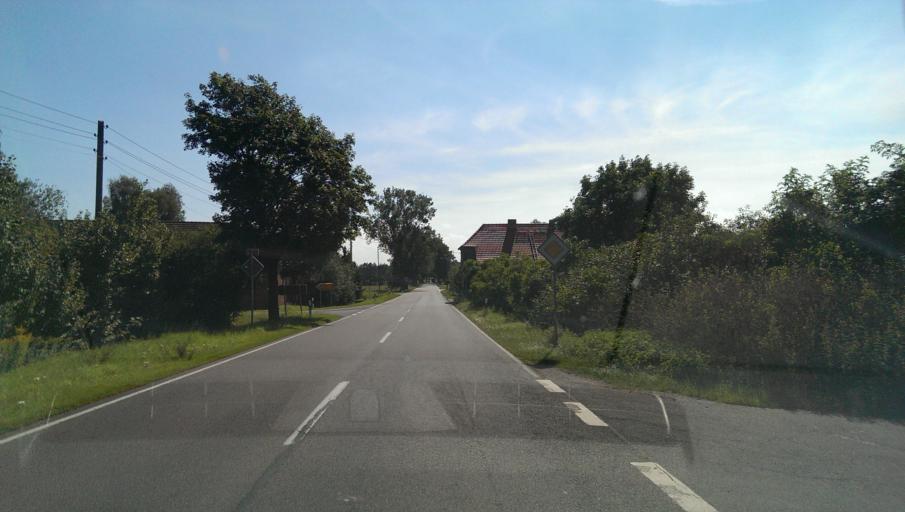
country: DE
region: Saxony-Anhalt
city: Kropstadt
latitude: 51.9681
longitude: 12.7555
